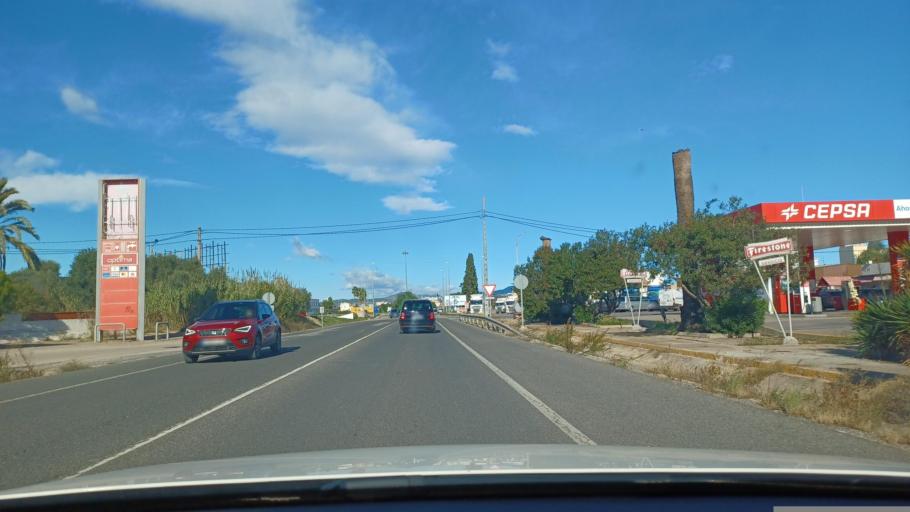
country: ES
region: Valencia
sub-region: Provincia de Castello
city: Vinaros
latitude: 40.4685
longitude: 0.4648
